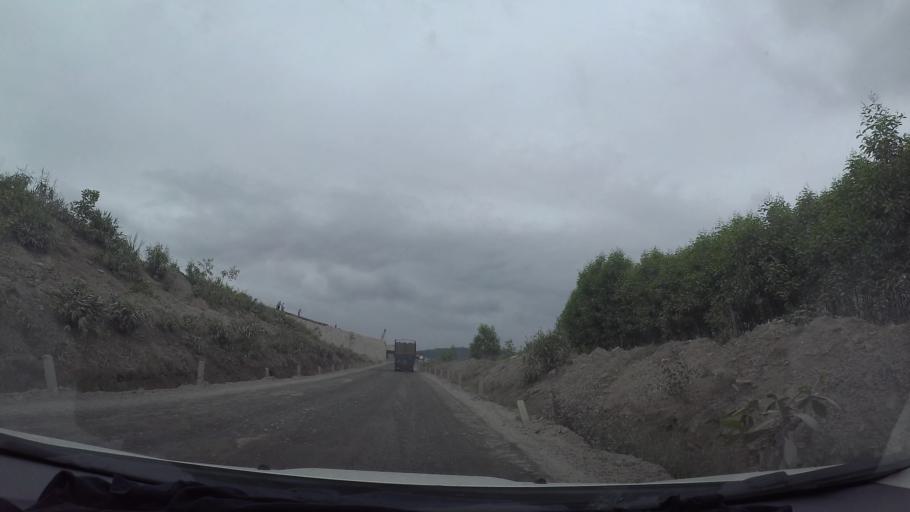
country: VN
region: Da Nang
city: Lien Chieu
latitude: 16.0957
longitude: 108.0884
